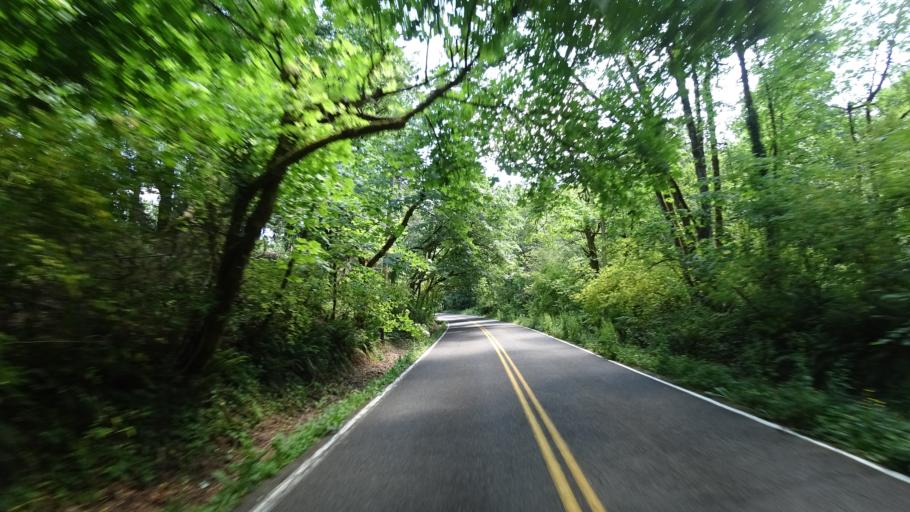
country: US
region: Oregon
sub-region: Clackamas County
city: Lake Oswego
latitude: 45.4434
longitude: -122.6988
